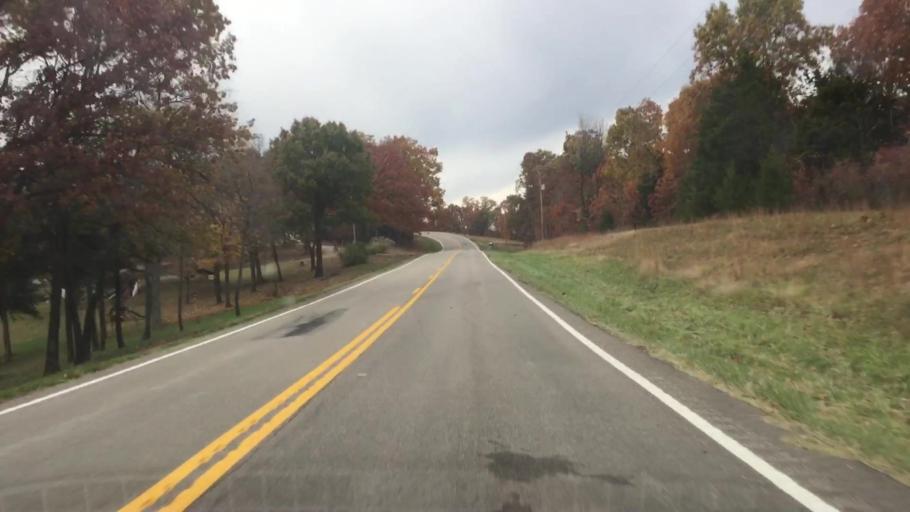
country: US
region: Missouri
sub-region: Gasconade County
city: Hermann
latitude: 38.7120
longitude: -91.6355
